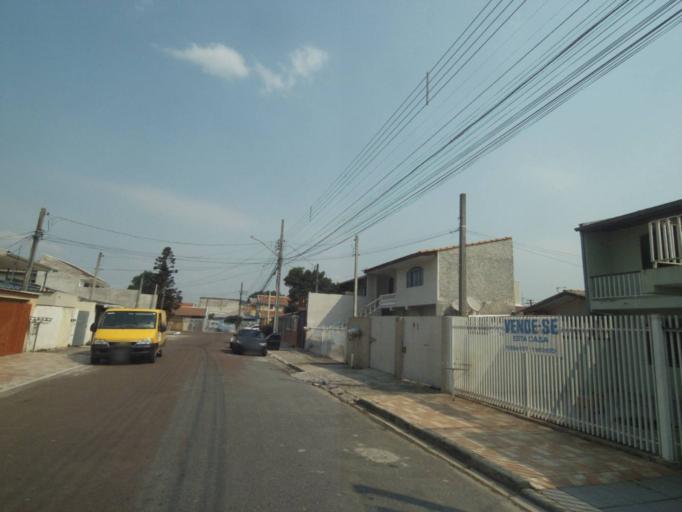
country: BR
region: Parana
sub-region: Sao Jose Dos Pinhais
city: Sao Jose dos Pinhais
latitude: -25.5268
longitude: -49.2331
